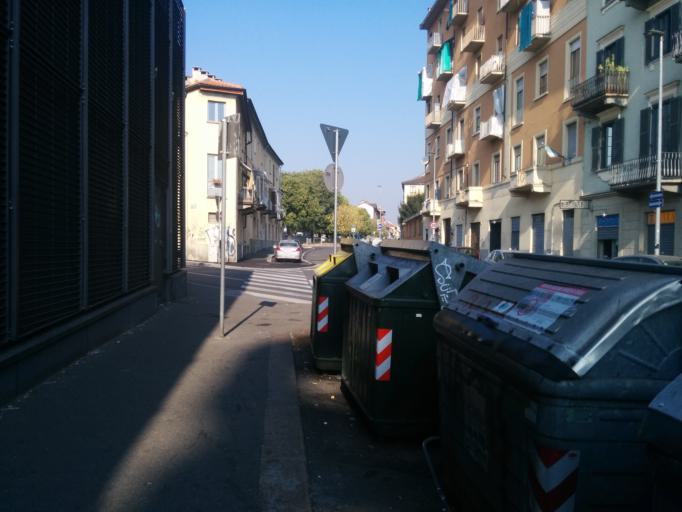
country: IT
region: Piedmont
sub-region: Provincia di Torino
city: Turin
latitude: 45.0910
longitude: 7.6764
